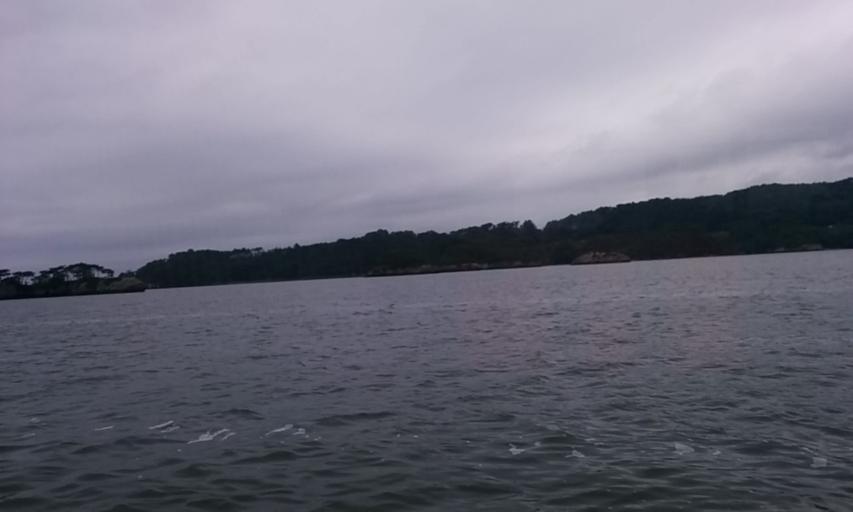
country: JP
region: Miyagi
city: Matsushima
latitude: 38.3586
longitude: 141.0715
